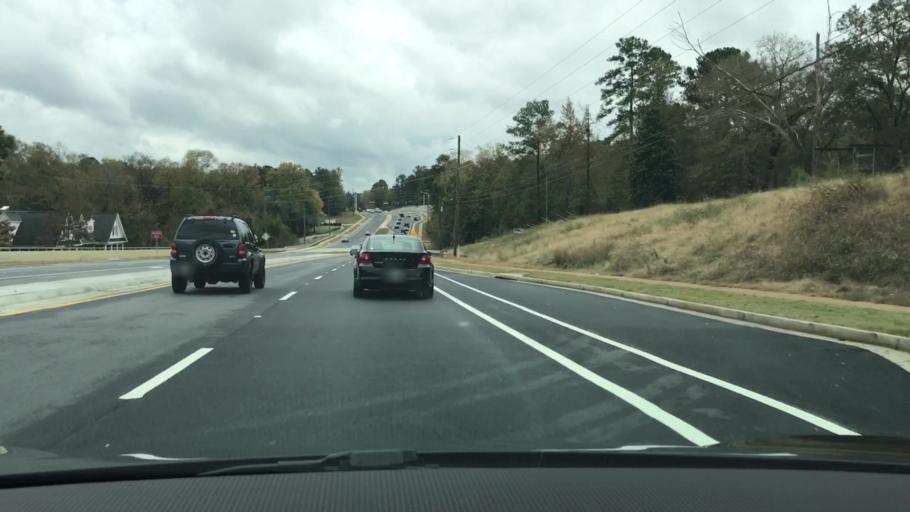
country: US
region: Georgia
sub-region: Oconee County
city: Watkinsville
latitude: 33.9039
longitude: -83.4638
